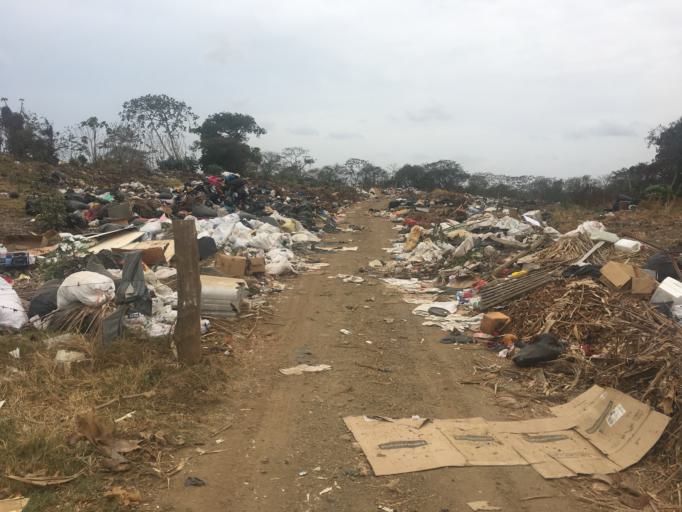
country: PA
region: Los Santos
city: Pedasi
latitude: 7.5480
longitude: -80.0810
